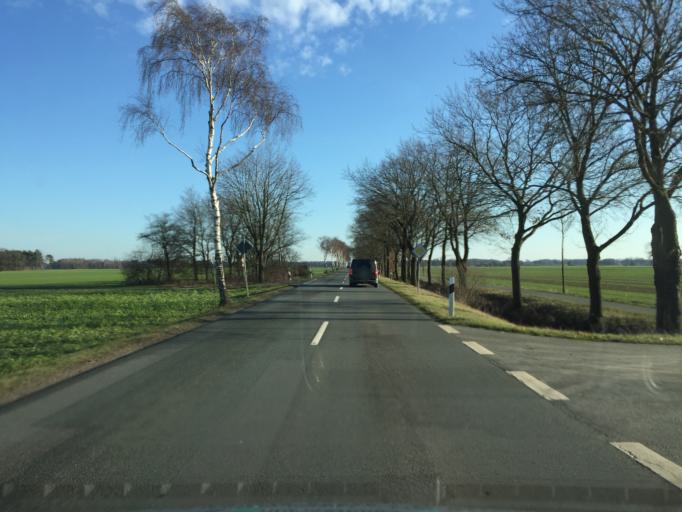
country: DE
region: Lower Saxony
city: Estorf
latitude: 52.5584
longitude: 9.1654
